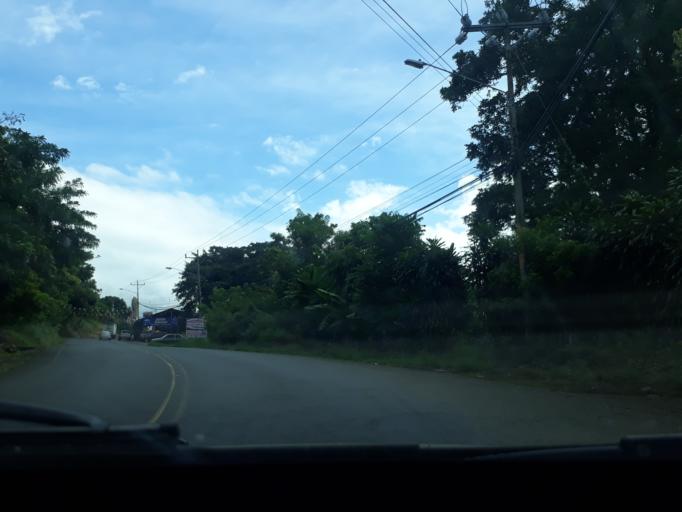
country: CR
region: Alajuela
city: Naranjo
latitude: 10.0397
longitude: -84.3470
